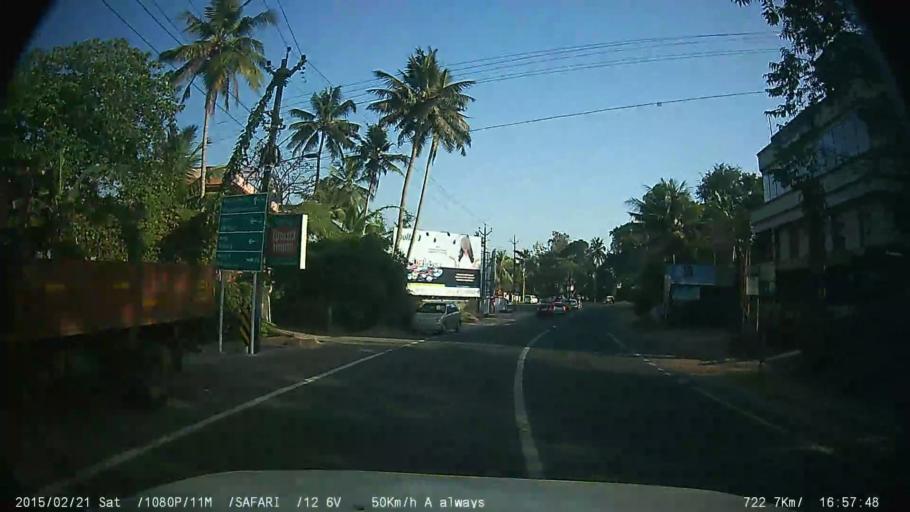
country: IN
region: Kerala
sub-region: Kottayam
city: Changanacheri
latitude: 9.4520
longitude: 76.5450
